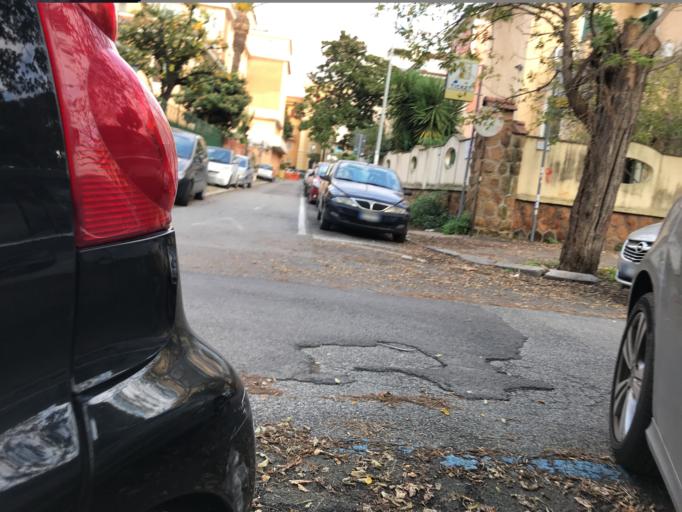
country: IT
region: Latium
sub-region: Citta metropolitana di Roma Capitale
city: Rome
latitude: 41.8995
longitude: 12.5091
